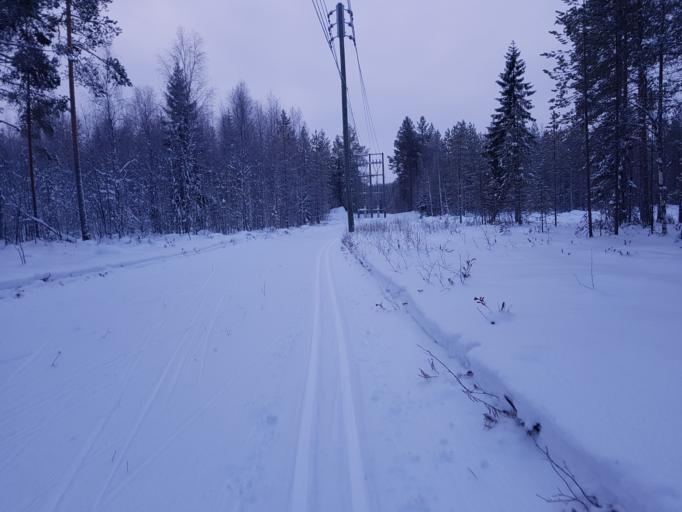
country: FI
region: Kainuu
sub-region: Kehys-Kainuu
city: Kuhmo
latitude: 64.1165
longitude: 29.5701
